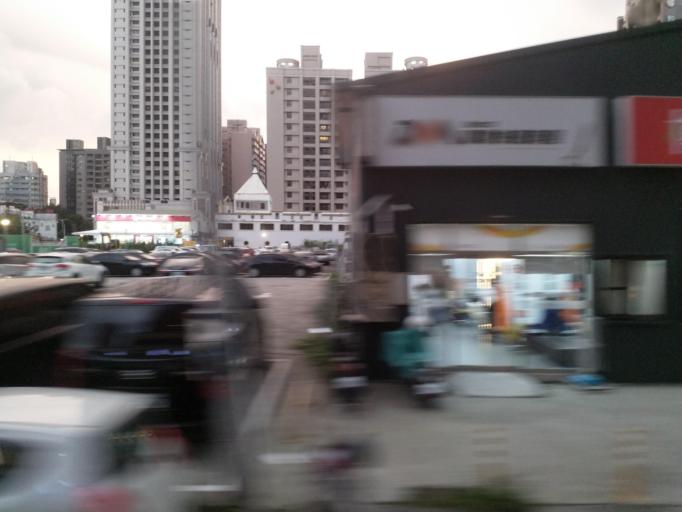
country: TW
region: Kaohsiung
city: Kaohsiung
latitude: 22.6849
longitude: 120.3122
